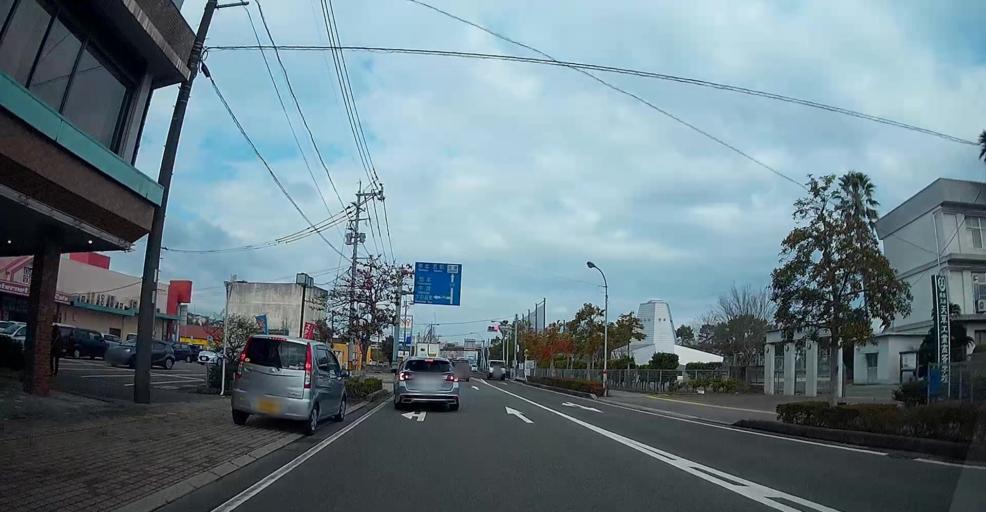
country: JP
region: Kumamoto
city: Hondo
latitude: 32.4460
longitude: 130.2017
